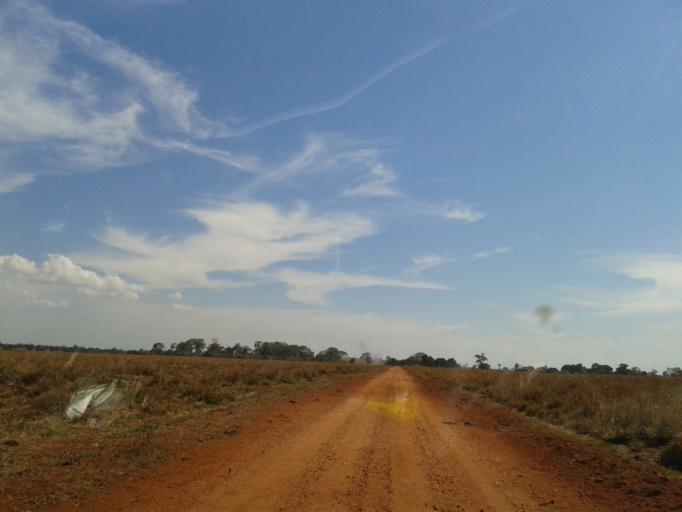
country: BR
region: Minas Gerais
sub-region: Santa Vitoria
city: Santa Vitoria
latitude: -18.6396
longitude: -49.9921
